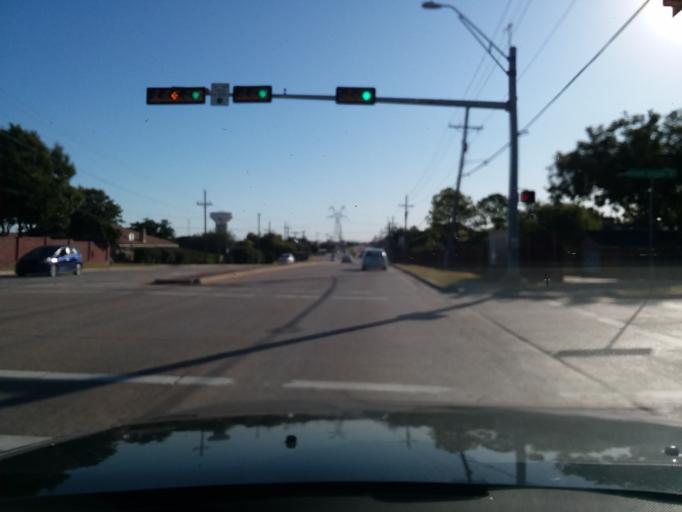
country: US
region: Texas
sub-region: Denton County
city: Highland Village
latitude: 33.0714
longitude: -97.0406
